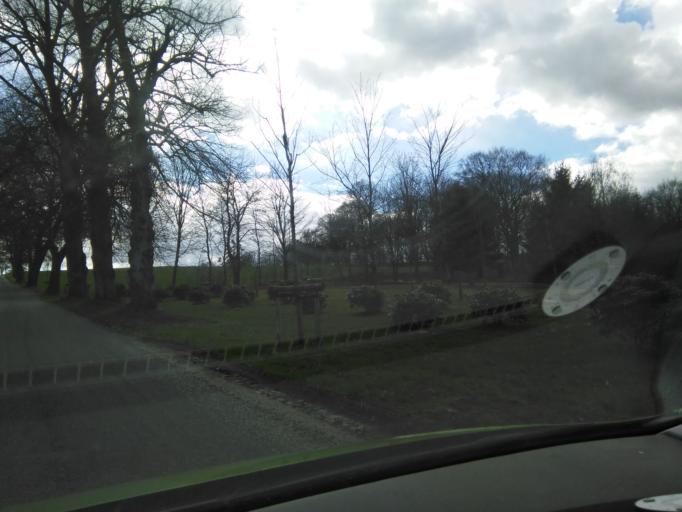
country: DK
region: Central Jutland
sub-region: Arhus Kommune
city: Kolt
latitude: 56.1377
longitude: 10.0771
